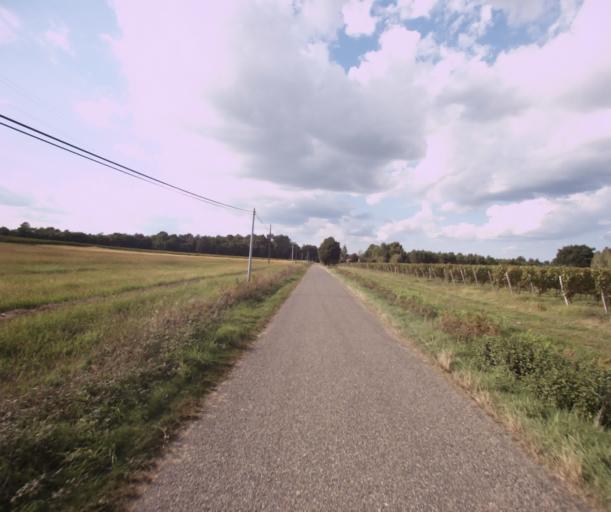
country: FR
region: Midi-Pyrenees
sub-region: Departement du Gers
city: Cazaubon
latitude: 43.8920
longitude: -0.0428
